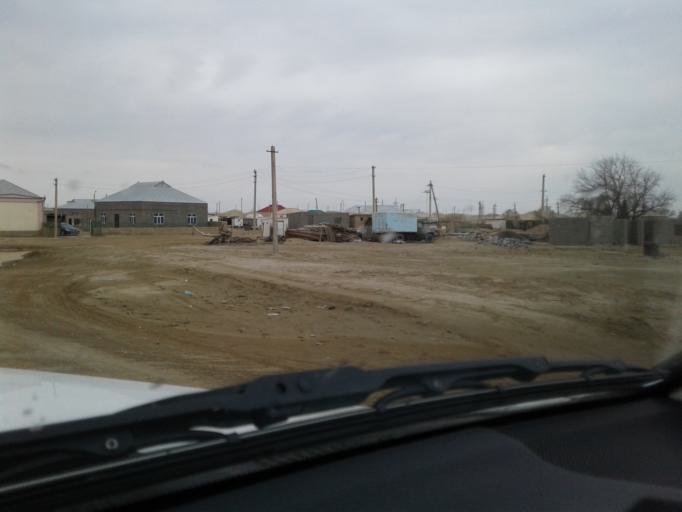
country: TM
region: Ahal
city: Abadan
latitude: 38.7600
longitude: 58.4919
